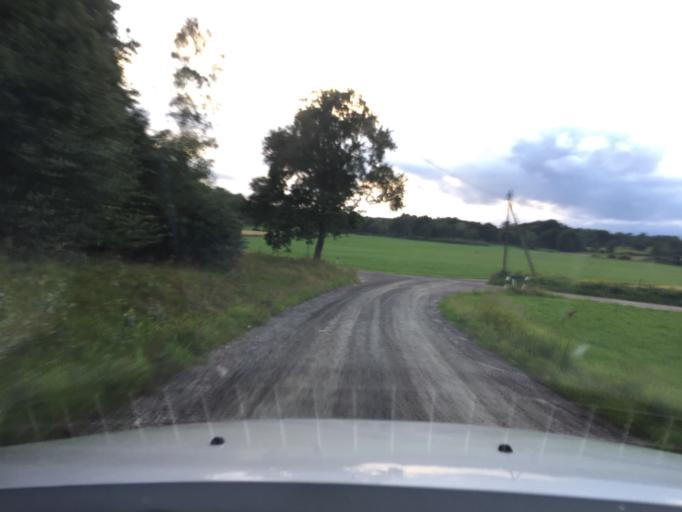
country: SE
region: Skane
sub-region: Hassleholms Kommun
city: Sosdala
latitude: 56.0629
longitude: 13.6604
